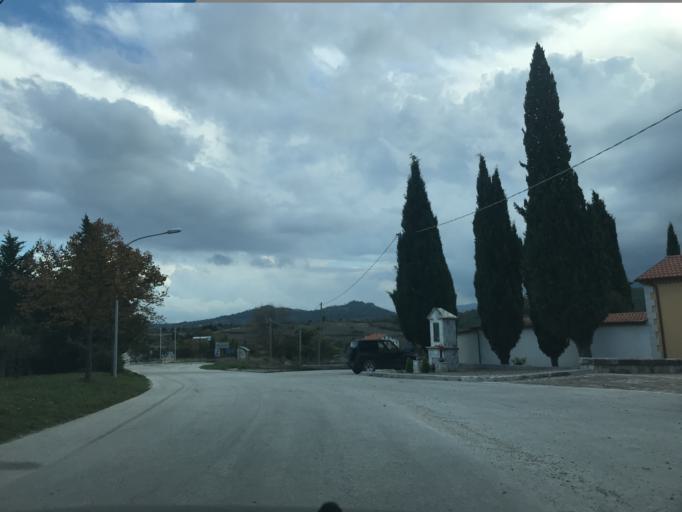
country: IT
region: Molise
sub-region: Provincia di Isernia
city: Bagnoli del Trigno
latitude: 41.6978
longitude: 14.4604
